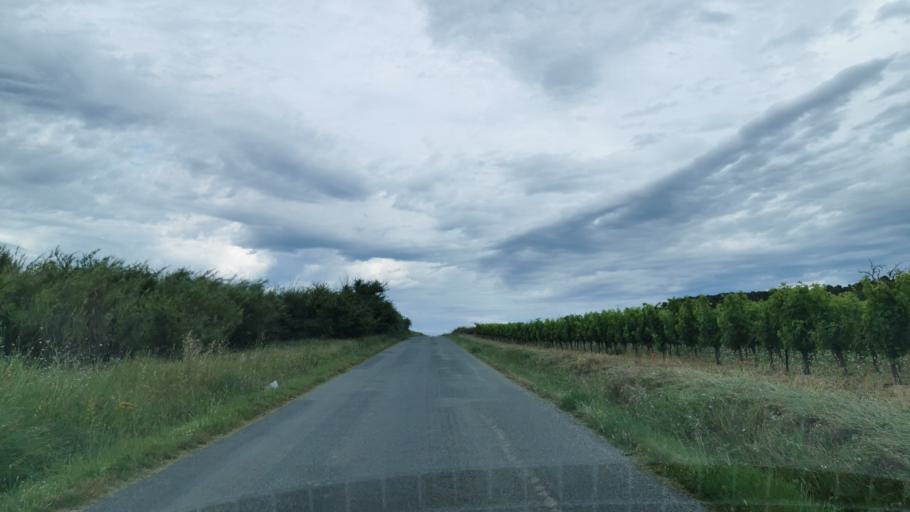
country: FR
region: Languedoc-Roussillon
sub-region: Departement de l'Aude
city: Marcorignan
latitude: 43.2215
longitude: 2.9352
